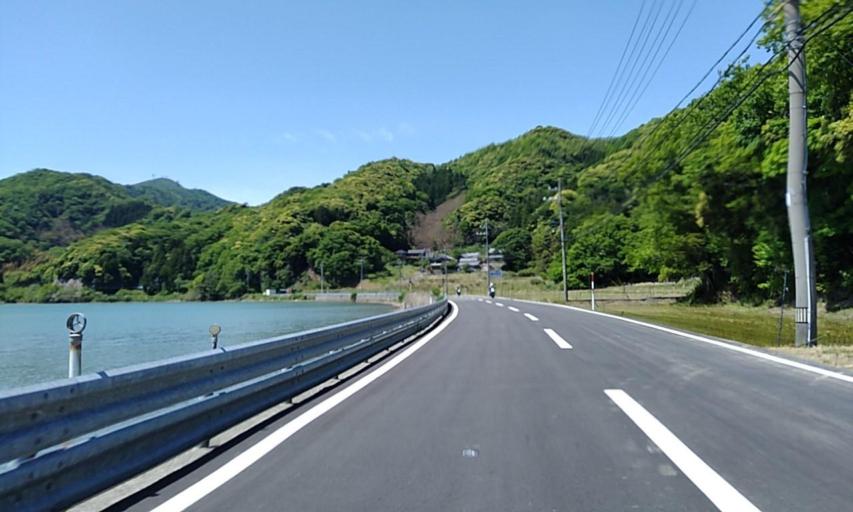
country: JP
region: Fukui
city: Obama
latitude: 35.5360
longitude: 135.7646
